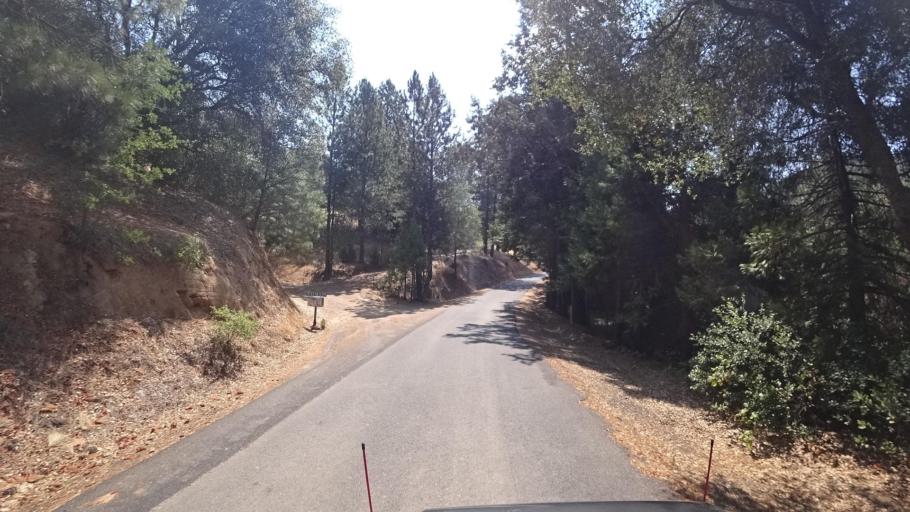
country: US
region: California
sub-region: Mariposa County
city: Midpines
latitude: 37.7012
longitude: -120.1356
